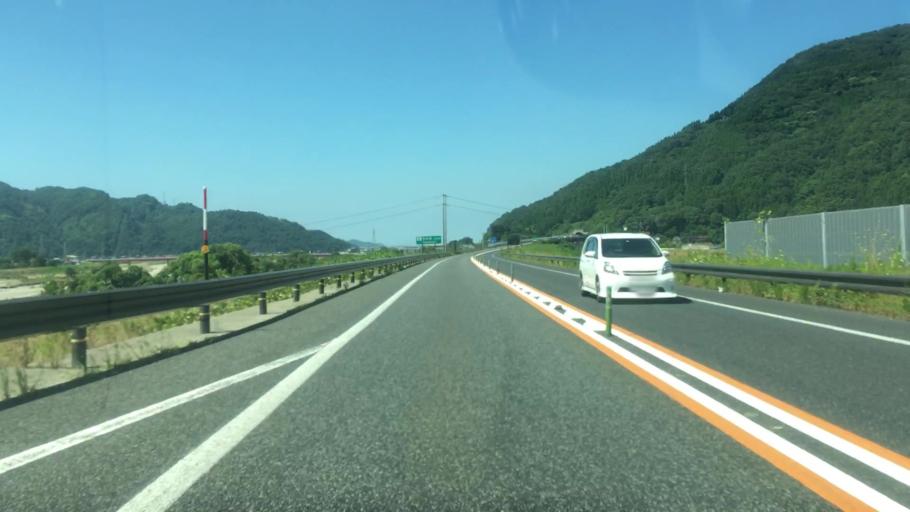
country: JP
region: Tottori
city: Tottori
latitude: 35.4005
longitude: 134.2050
